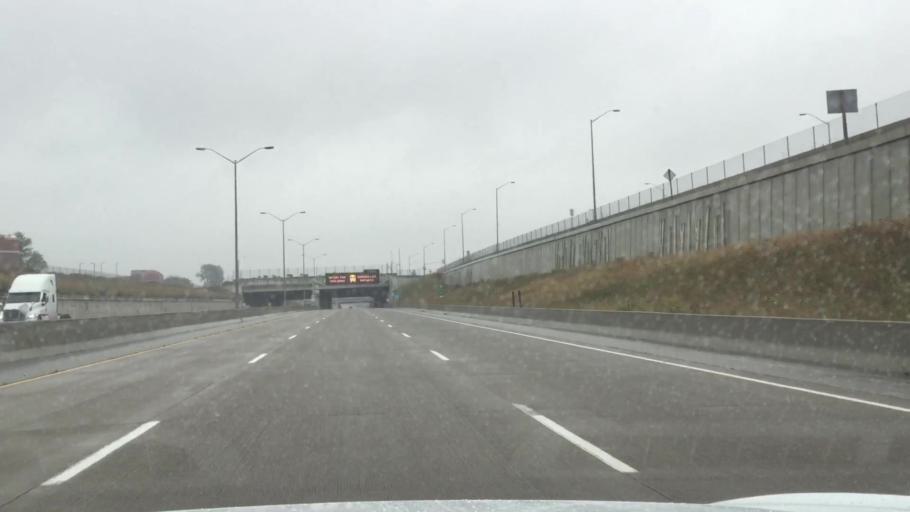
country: CA
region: Ontario
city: Windsor
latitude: 42.2431
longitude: -83.0176
